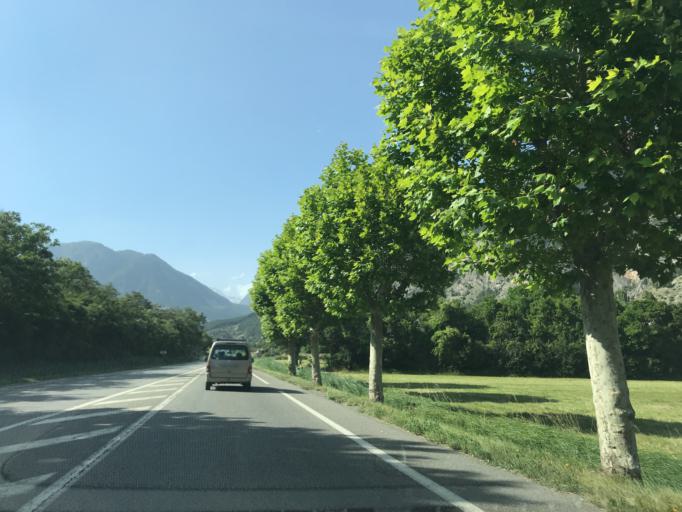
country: FR
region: Provence-Alpes-Cote d'Azur
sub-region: Departement des Hautes-Alpes
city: Saint-Martin-de-Queyrieres
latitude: 44.7552
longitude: 6.5752
